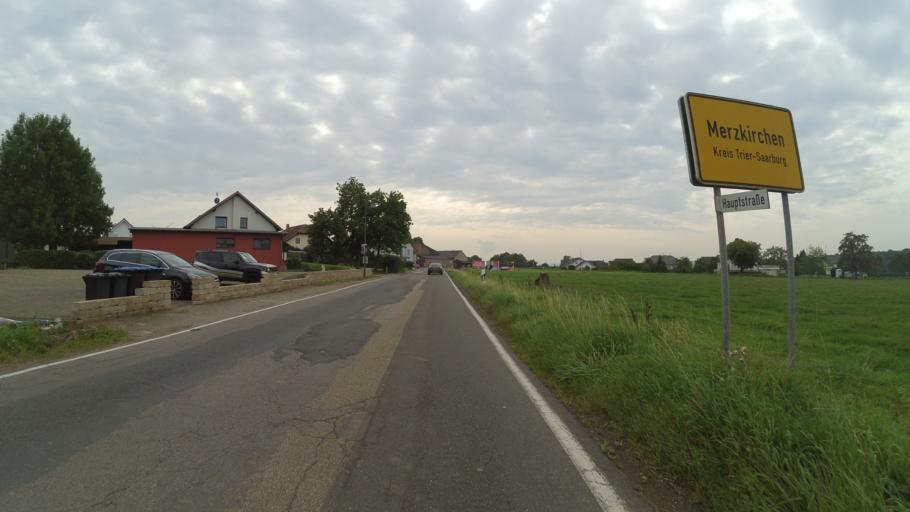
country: DE
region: Rheinland-Pfalz
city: Merzkirchen
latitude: 49.5800
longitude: 6.4781
